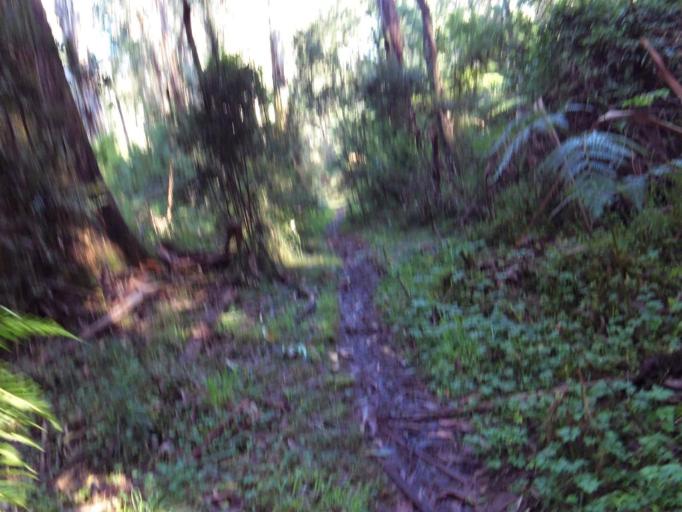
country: AU
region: Victoria
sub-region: Cardinia
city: Emerald
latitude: -37.9180
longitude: 145.4381
